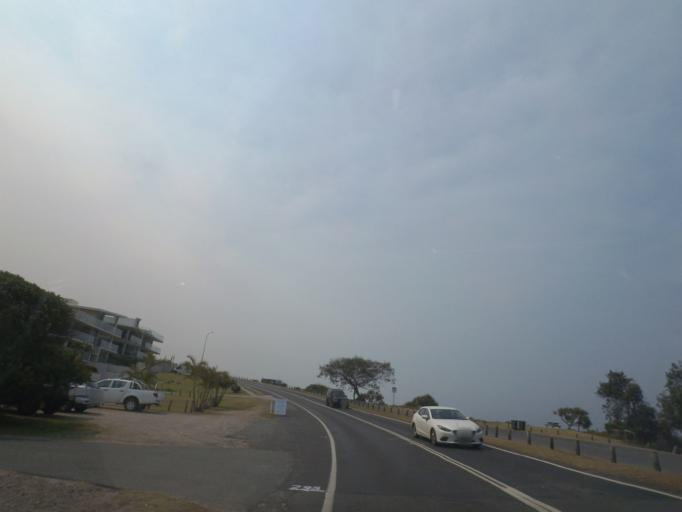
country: AU
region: New South Wales
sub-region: Tweed
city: Casuarina
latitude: -28.3359
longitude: 153.5744
